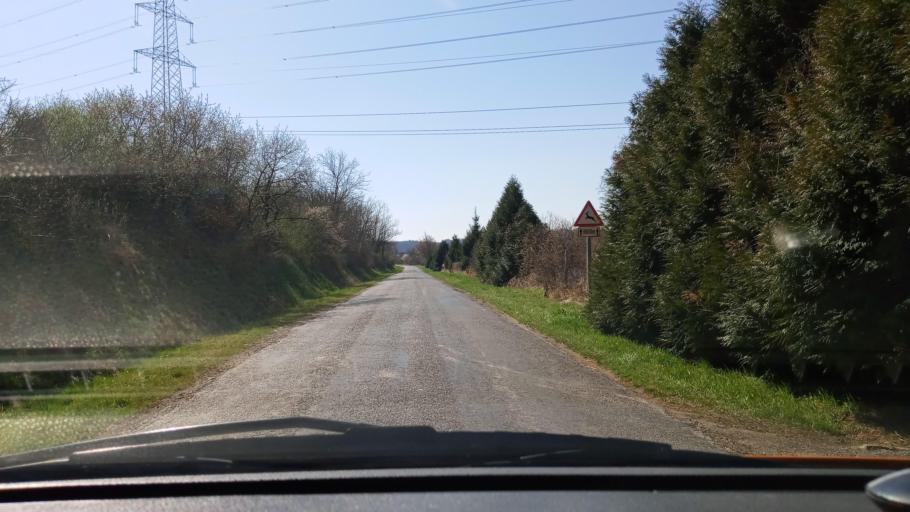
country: HU
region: Baranya
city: Kozarmisleny
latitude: 46.0458
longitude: 18.3825
